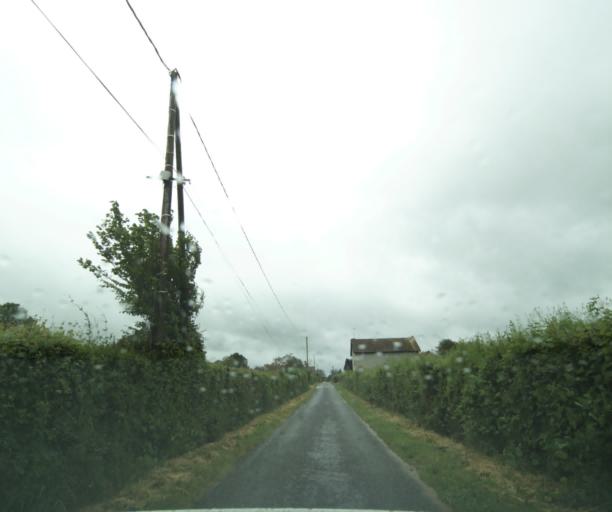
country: FR
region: Bourgogne
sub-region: Departement de Saone-et-Loire
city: Charolles
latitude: 46.4871
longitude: 4.4160
